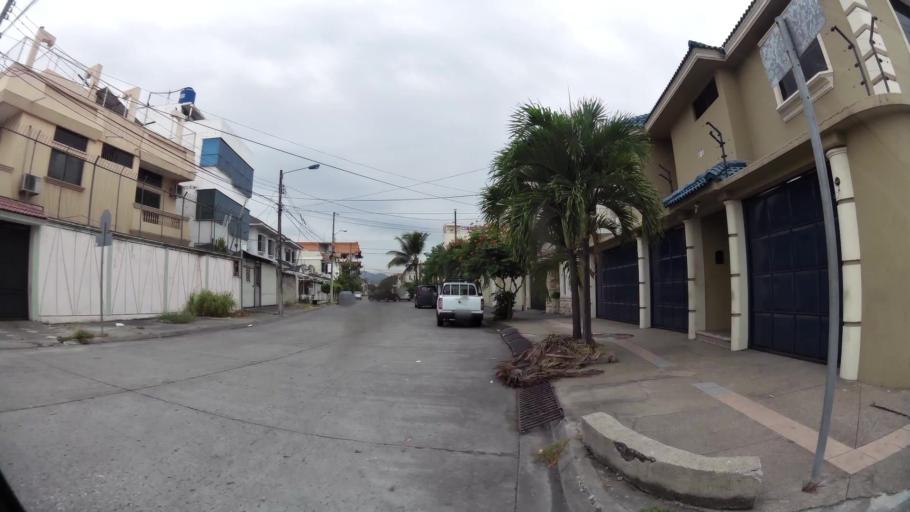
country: EC
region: Guayas
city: Eloy Alfaro
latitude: -2.1488
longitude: -79.8875
